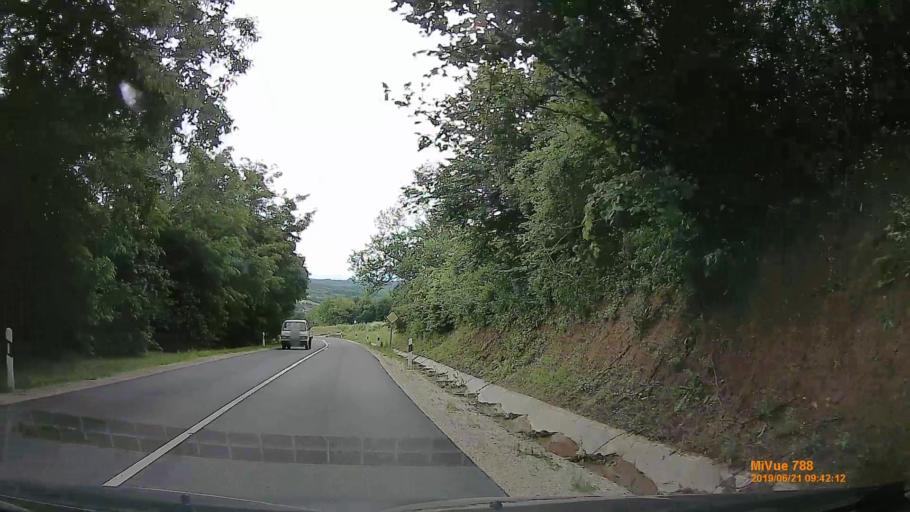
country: HU
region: Somogy
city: Taszar
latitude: 46.2902
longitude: 17.9641
